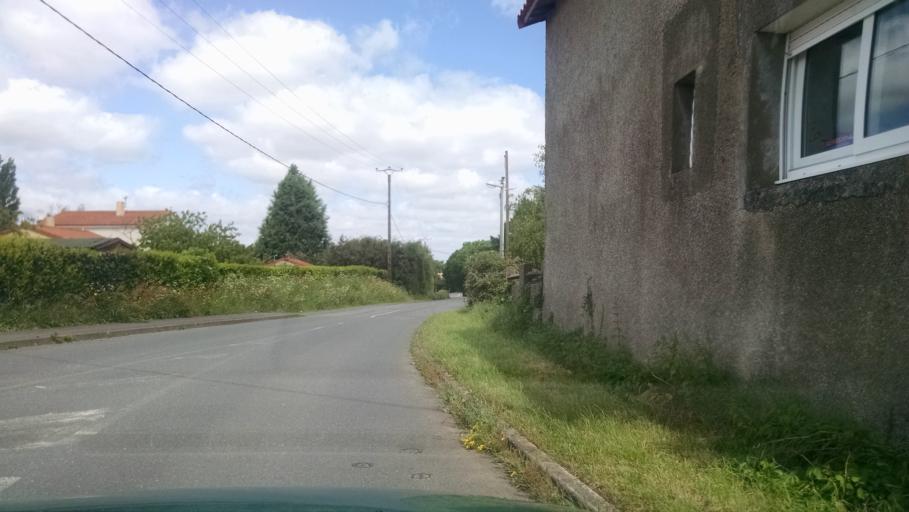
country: FR
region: Pays de la Loire
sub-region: Departement de la Loire-Atlantique
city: Gorges
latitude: 47.0903
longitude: -1.3102
